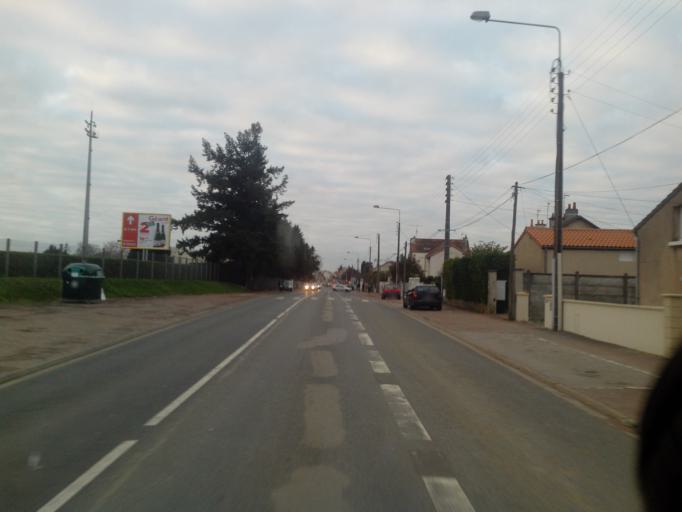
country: FR
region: Poitou-Charentes
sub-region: Departement de la Vienne
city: Saint-Benoit
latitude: 46.5711
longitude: 0.3743
